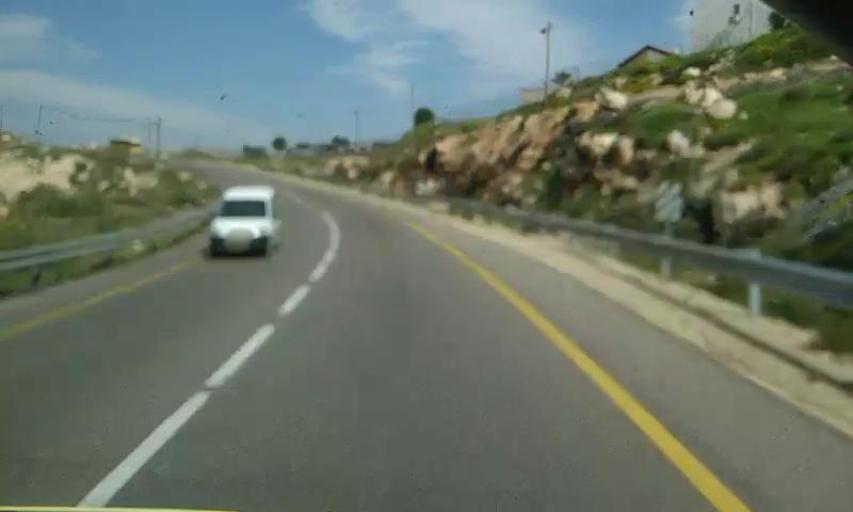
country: PS
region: West Bank
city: Az Zahiriyah
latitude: 31.3903
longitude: 35.0139
